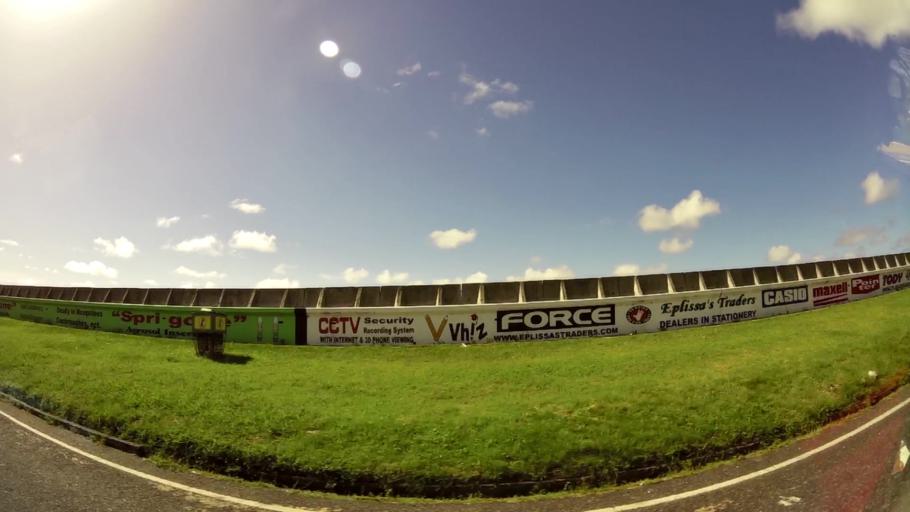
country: GY
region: Demerara-Mahaica
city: Georgetown
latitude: 6.8253
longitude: -58.1343
